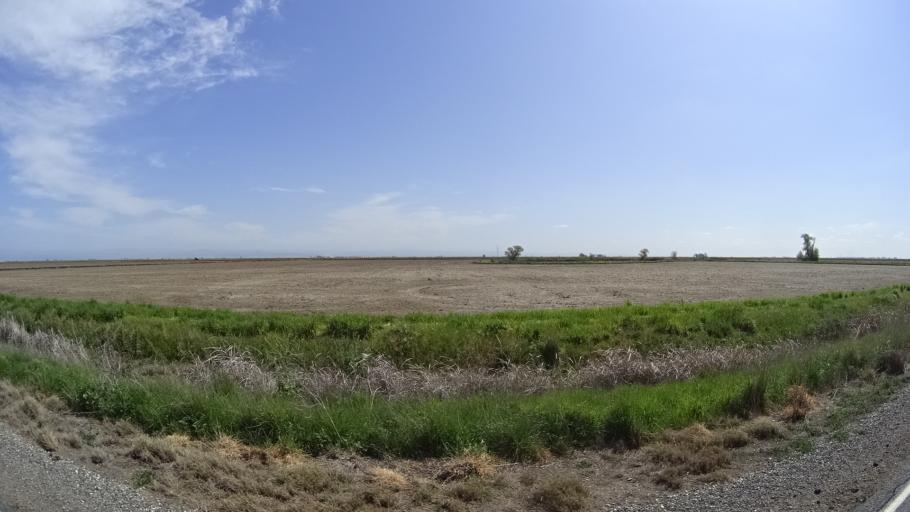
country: US
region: California
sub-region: Butte County
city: Biggs
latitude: 39.4798
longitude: -121.8575
